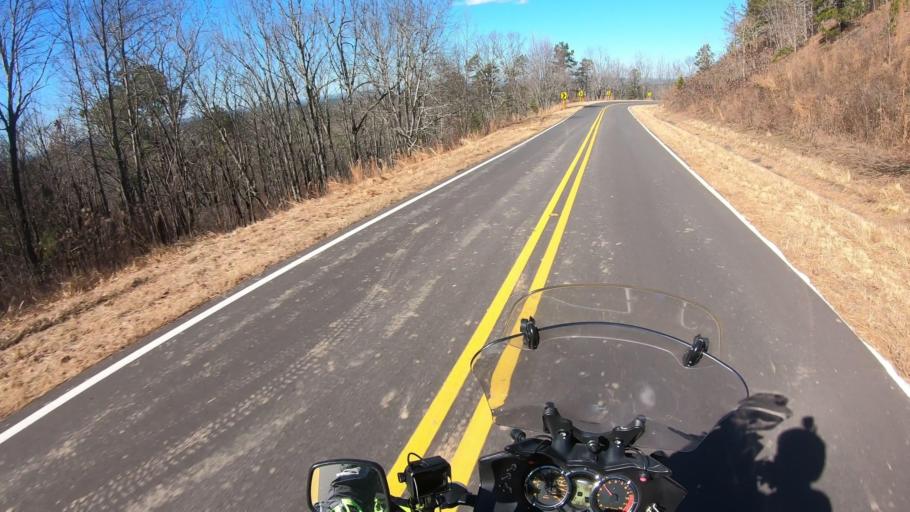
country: US
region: Alabama
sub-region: Clay County
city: Ashland
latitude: 33.4086
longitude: -85.8757
